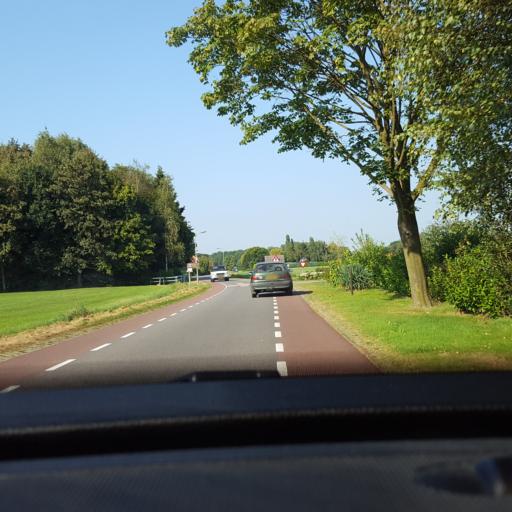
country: NL
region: Gelderland
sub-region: Gemeente Lochem
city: Barchem
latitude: 52.0679
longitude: 6.4493
